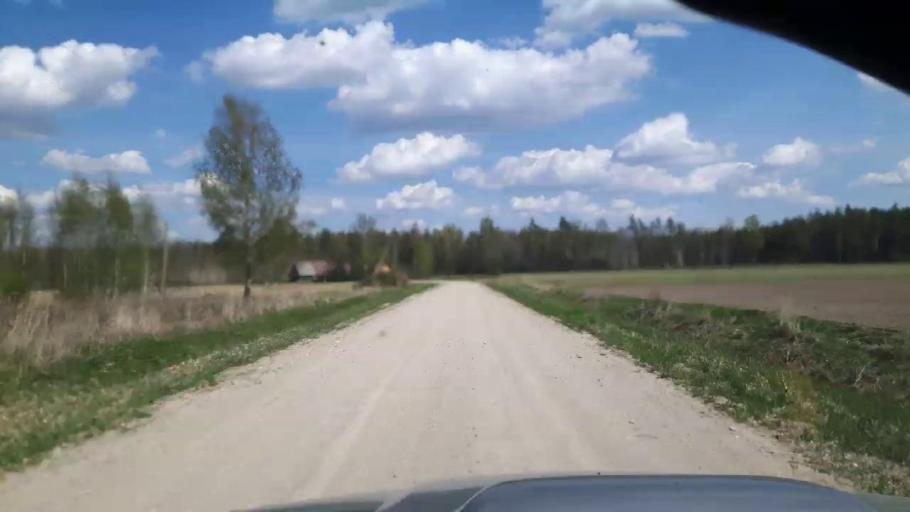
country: EE
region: Paernumaa
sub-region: Tootsi vald
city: Tootsi
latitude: 58.4739
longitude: 24.9034
